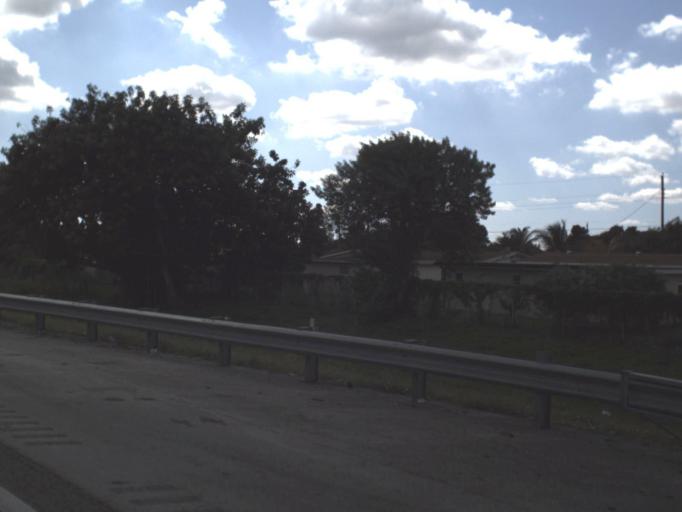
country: US
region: Florida
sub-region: Broward County
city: Miramar
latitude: 25.9861
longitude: -80.2296
